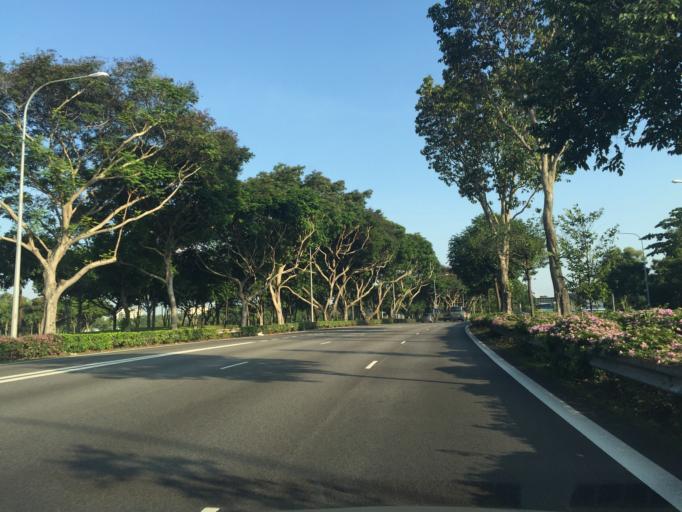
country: SG
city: Singapore
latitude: 1.3414
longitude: 103.9707
